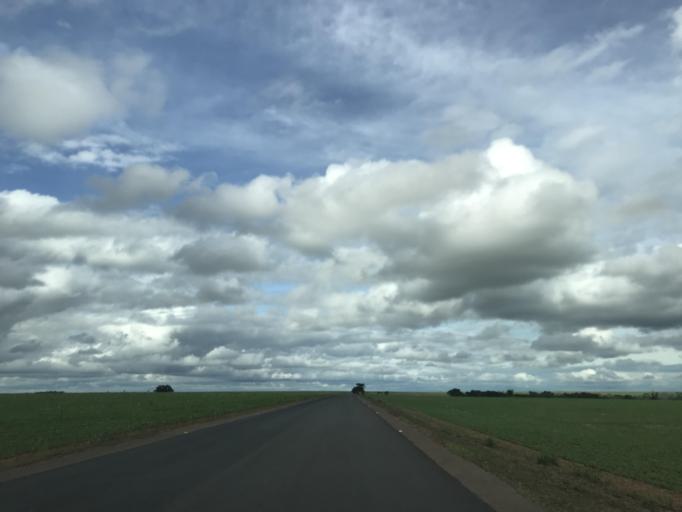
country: BR
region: Goias
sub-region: Vianopolis
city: Vianopolis
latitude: -16.9678
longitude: -48.6501
